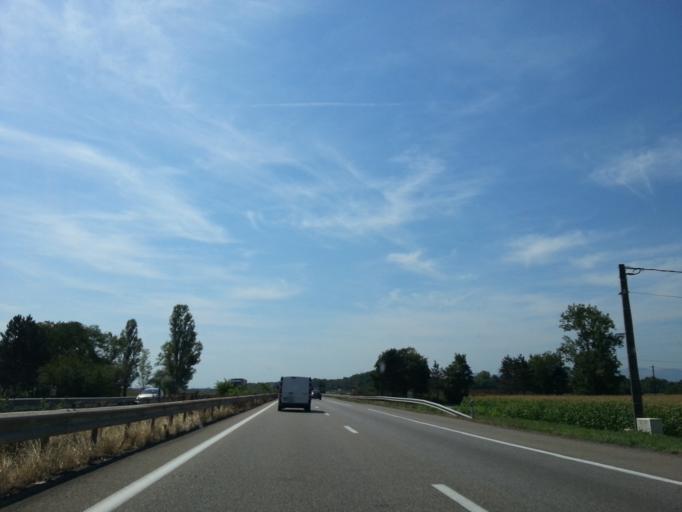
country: FR
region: Alsace
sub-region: Departement du Haut-Rhin
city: Ostheim
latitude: 48.1467
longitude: 7.3688
